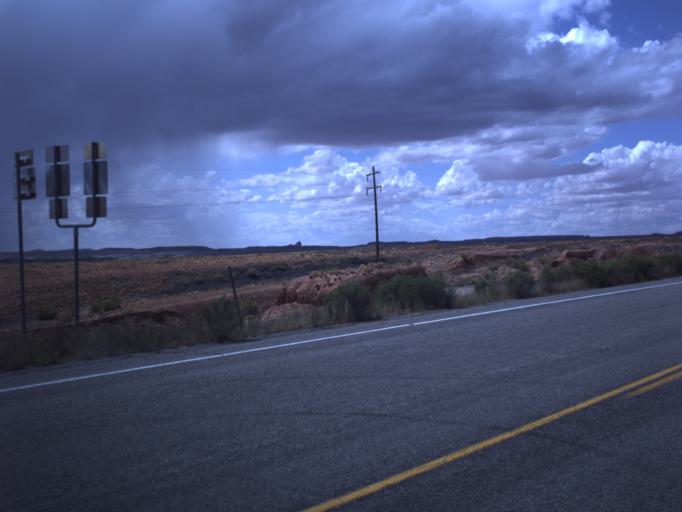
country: US
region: Utah
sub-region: San Juan County
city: Blanding
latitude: 37.2654
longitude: -109.6270
